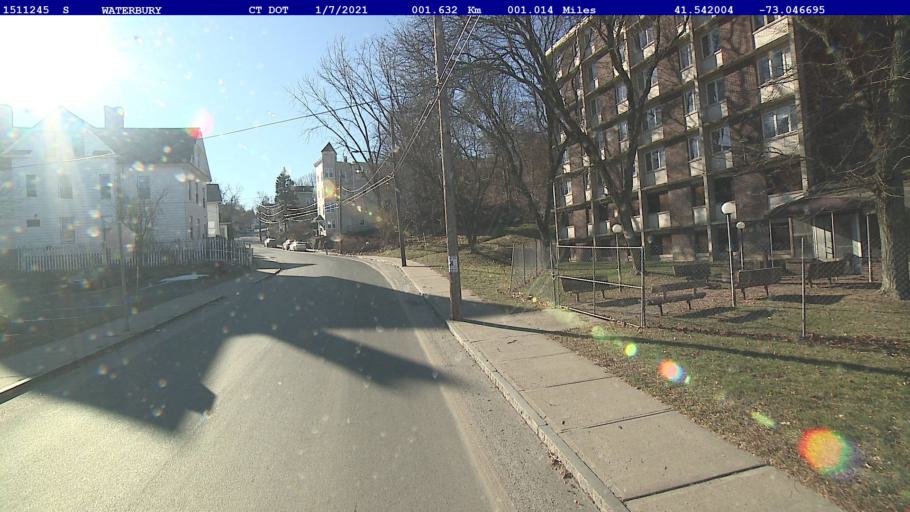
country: US
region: Connecticut
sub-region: New Haven County
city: Waterbury
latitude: 41.5420
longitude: -73.0467
